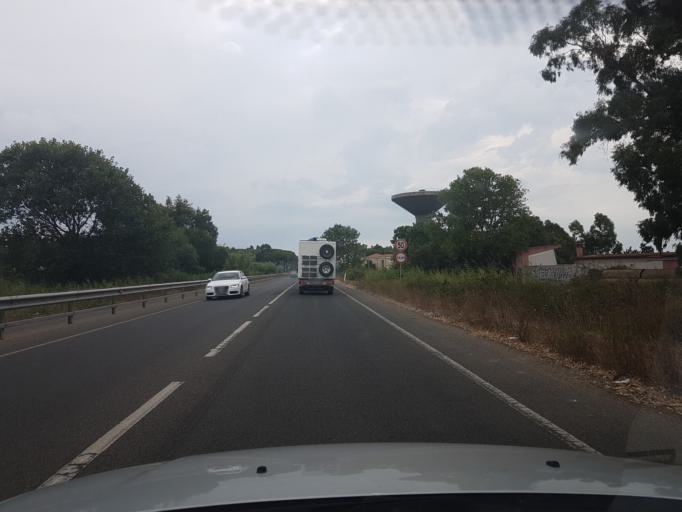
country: IT
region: Sardinia
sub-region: Provincia di Oristano
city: Cabras
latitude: 39.9091
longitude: 8.5244
